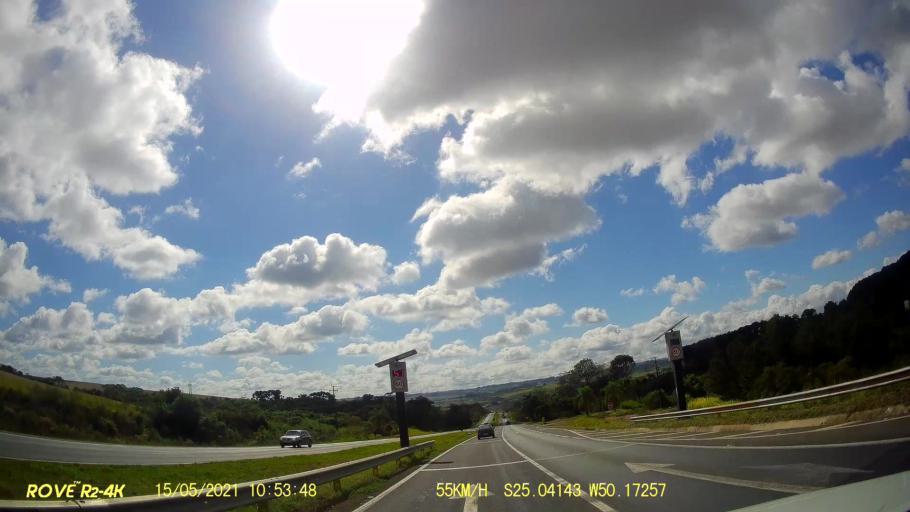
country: BR
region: Parana
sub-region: Ponta Grossa
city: Ponta Grossa
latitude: -25.0418
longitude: -50.1729
